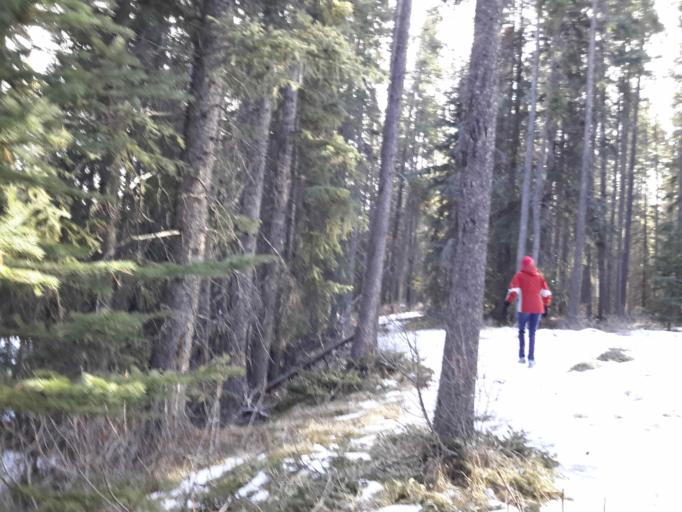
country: CA
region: Alberta
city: Banff
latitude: 51.2014
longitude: -115.5326
